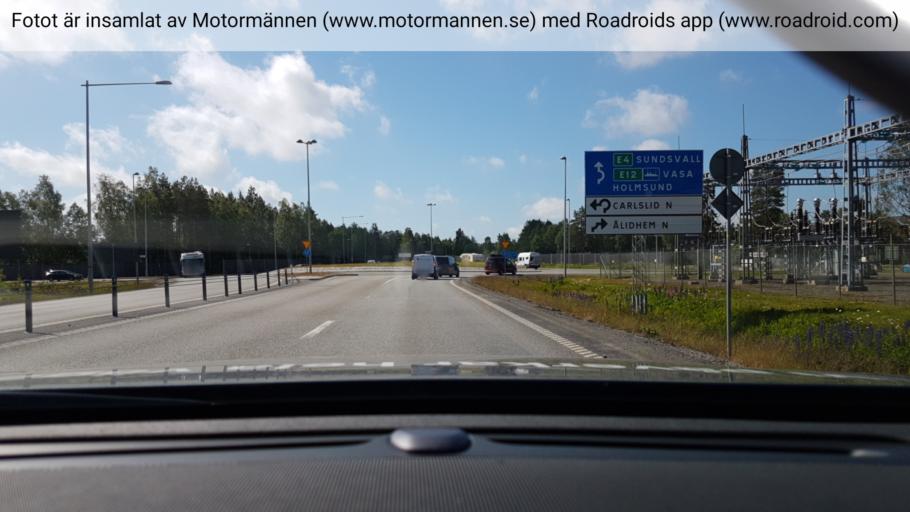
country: SE
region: Vaesterbotten
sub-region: Umea Kommun
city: Umea
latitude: 63.8118
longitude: 20.3259
